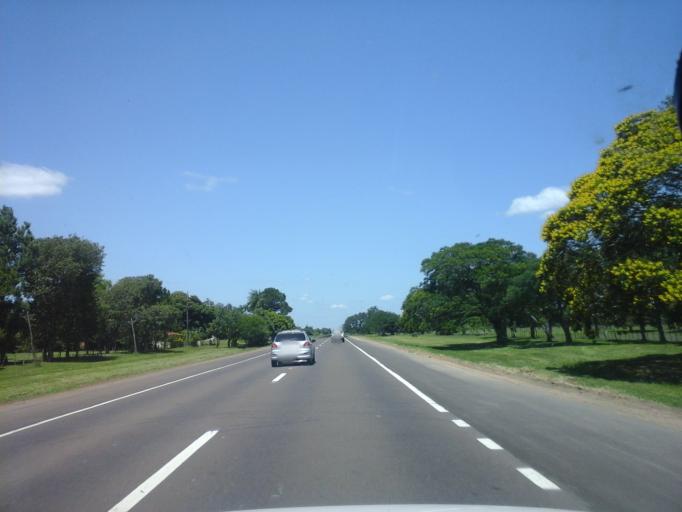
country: AR
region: Corrientes
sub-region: Departamento de Itati
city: Itati
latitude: -27.3671
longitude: -58.3566
